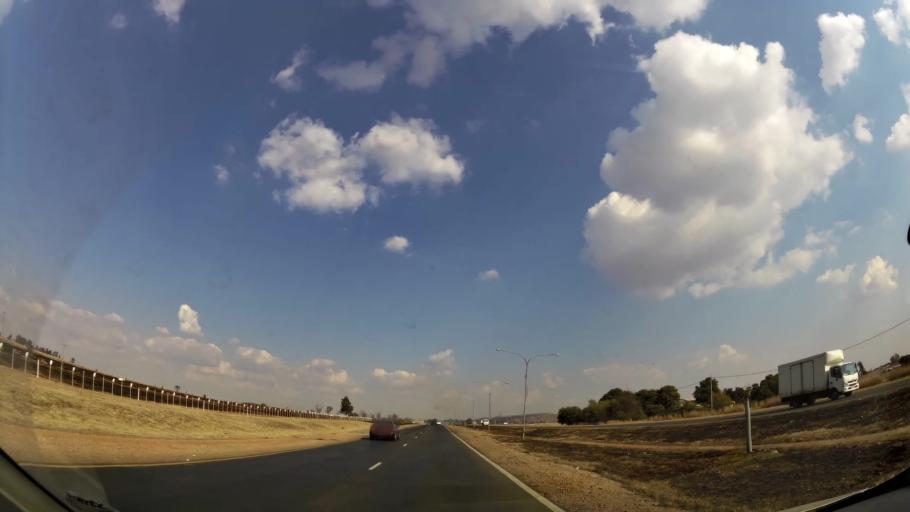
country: ZA
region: Gauteng
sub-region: Ekurhuleni Metropolitan Municipality
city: Brakpan
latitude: -26.3088
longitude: 28.3364
